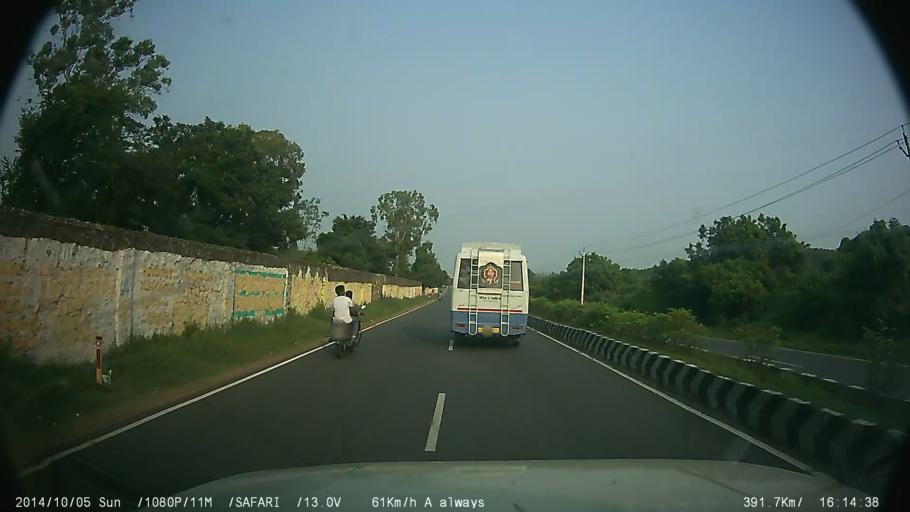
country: IN
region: Tamil Nadu
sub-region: Kancheepuram
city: Vandalur
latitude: 12.8724
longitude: 80.0961
